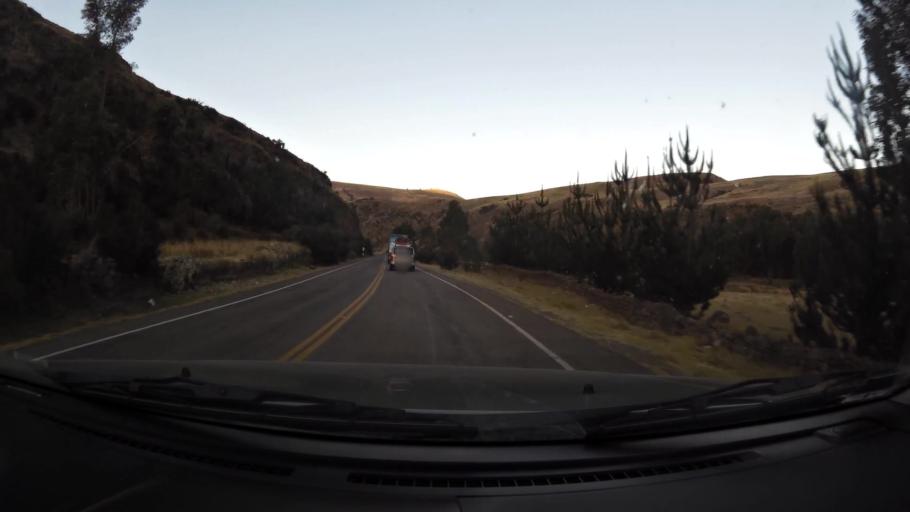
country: PE
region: Ayacucho
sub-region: Provincia de Huamanga
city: Vinchos
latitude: -13.3399
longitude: -74.3583
